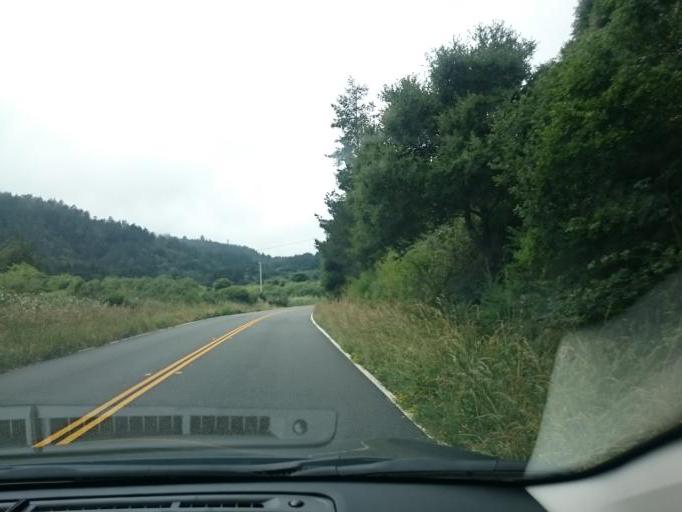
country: US
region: California
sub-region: Marin County
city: Lagunitas-Forest Knolls
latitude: 37.9708
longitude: -122.7287
